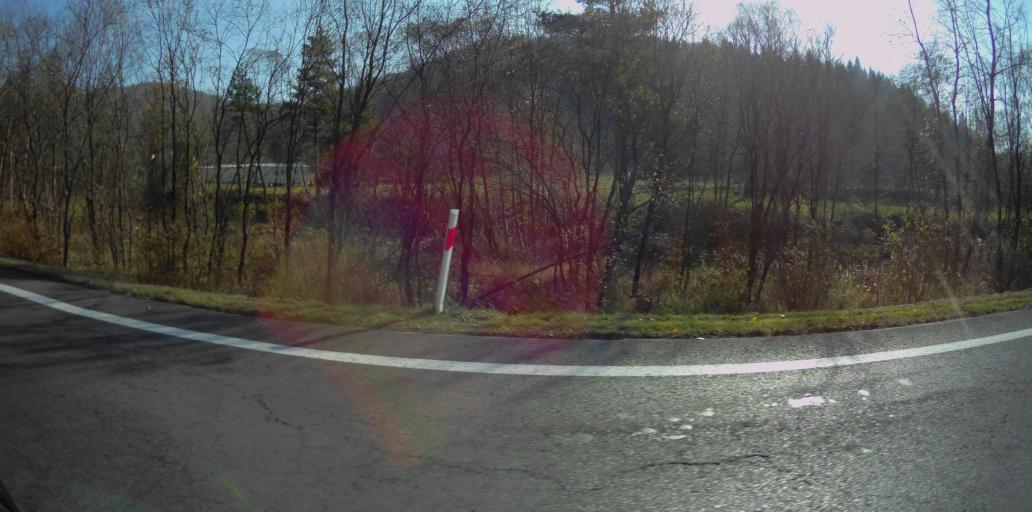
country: PL
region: Subcarpathian Voivodeship
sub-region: Powiat bieszczadzki
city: Ustrzyki Dolne
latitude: 49.4550
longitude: 22.6336
